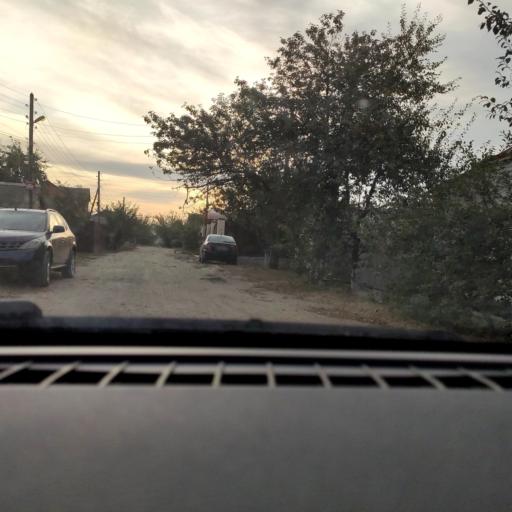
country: RU
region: Voronezj
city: Voronezh
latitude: 51.6665
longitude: 39.2885
